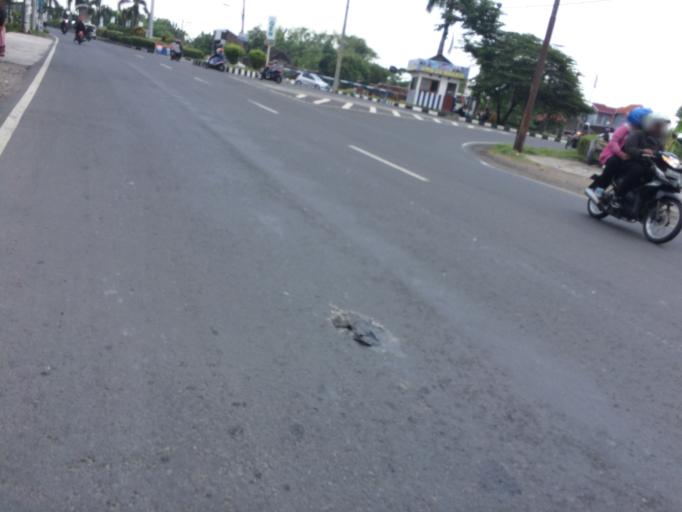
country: ID
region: Central Java
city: Grogol
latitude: -7.6109
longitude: 110.8188
